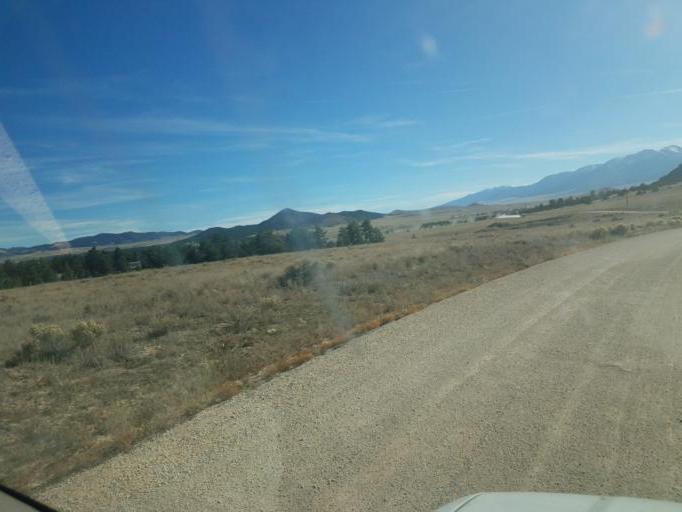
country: US
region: Colorado
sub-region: Custer County
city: Westcliffe
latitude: 38.2274
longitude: -105.4576
